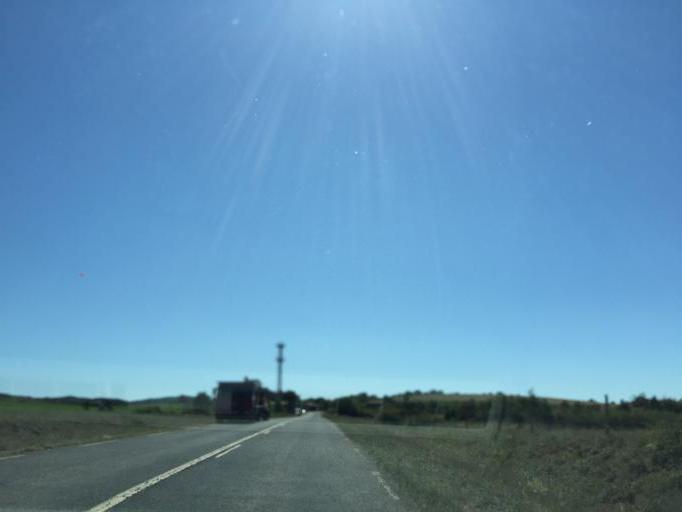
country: FR
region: Midi-Pyrenees
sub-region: Departement de l'Aveyron
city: La Cavalerie
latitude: 43.9075
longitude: 3.2598
